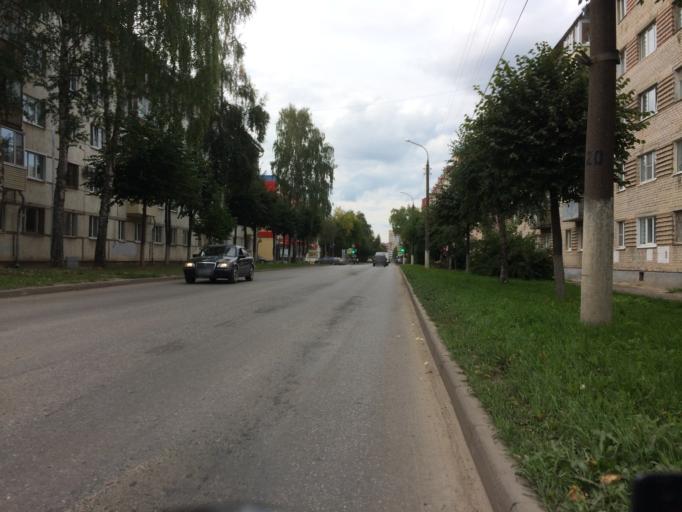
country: RU
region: Mariy-El
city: Yoshkar-Ola
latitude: 56.6347
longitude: 47.8720
